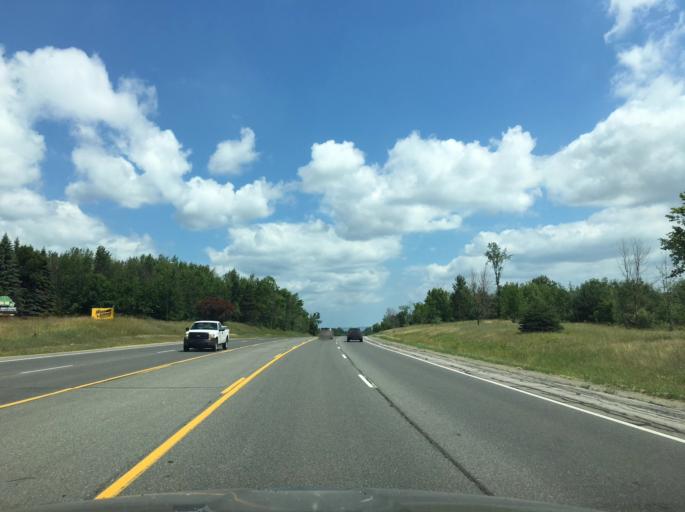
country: US
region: Michigan
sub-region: Grand Traverse County
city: Traverse City
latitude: 44.7017
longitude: -85.6556
